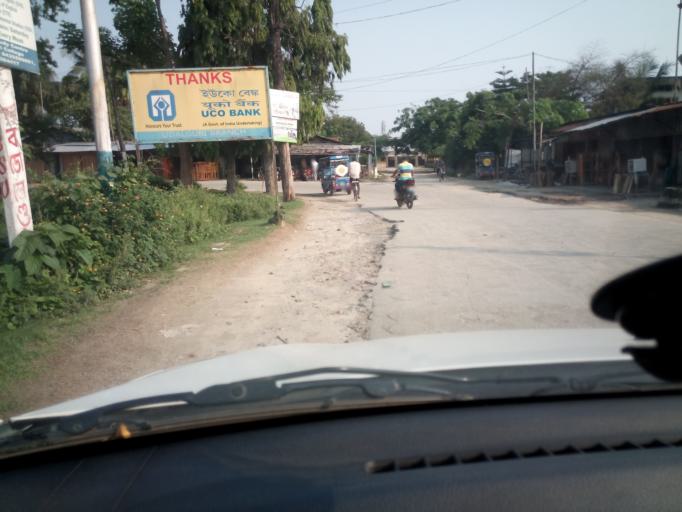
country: IN
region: Assam
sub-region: Udalguri
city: Udalguri
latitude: 26.7442
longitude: 92.0937
